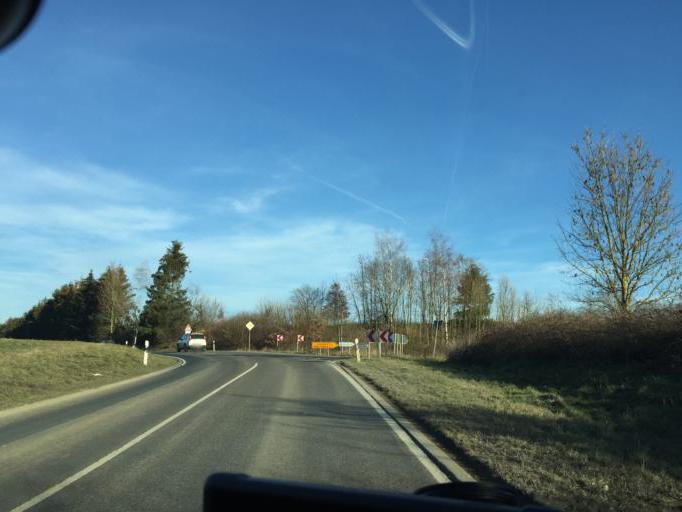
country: DE
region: Rheinland-Pfalz
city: Ruppach-Goldhausen
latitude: 50.4766
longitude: 7.8692
